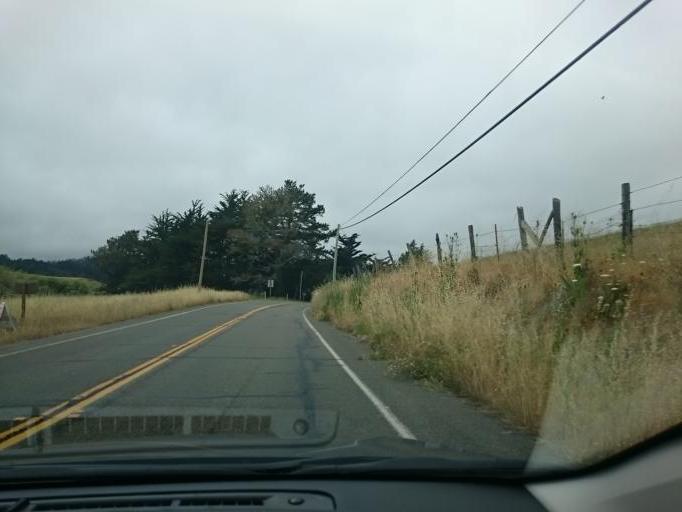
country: US
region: California
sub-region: Marin County
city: Inverness
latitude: 38.0579
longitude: -122.7996
